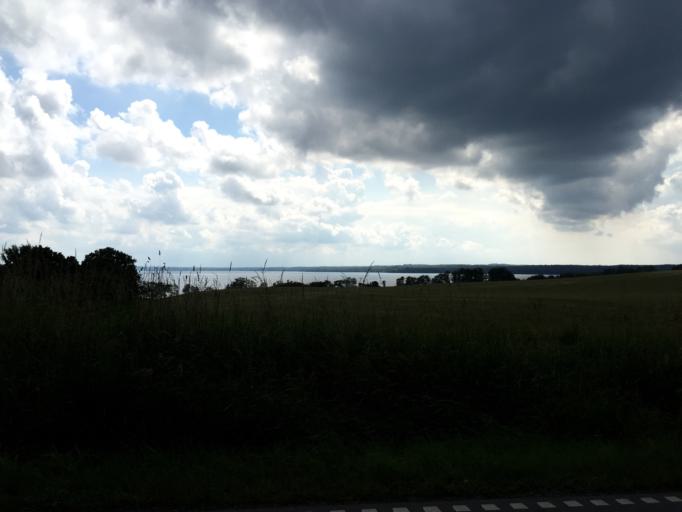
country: DK
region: Capital Region
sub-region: Helsingor Kommune
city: Hornbaek
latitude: 56.0370
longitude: 12.4189
